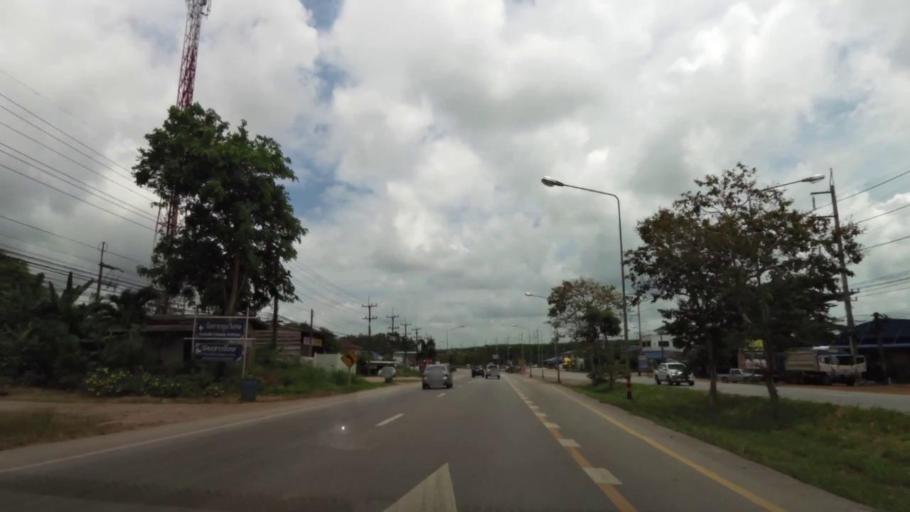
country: TH
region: Chanthaburi
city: Na Yai Am
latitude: 12.7865
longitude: 101.7907
